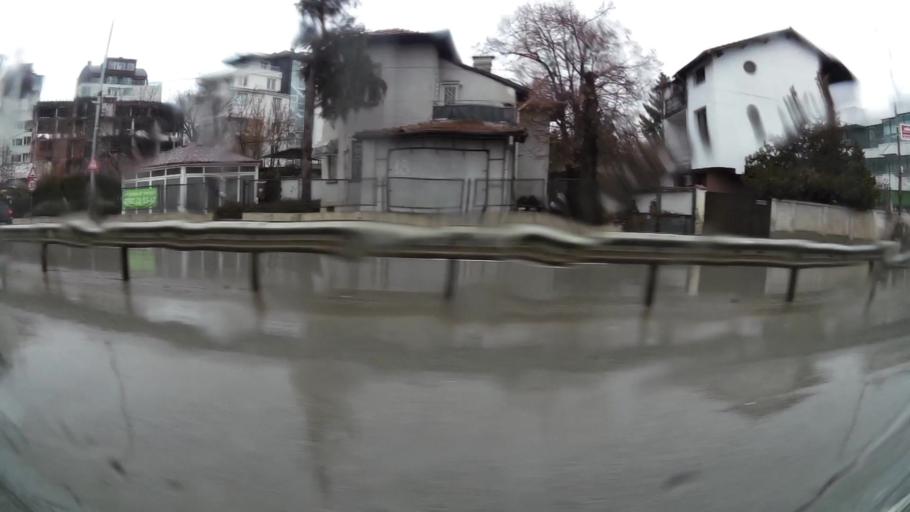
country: BG
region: Sofia-Capital
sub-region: Stolichna Obshtina
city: Sofia
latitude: 42.6561
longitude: 23.3363
